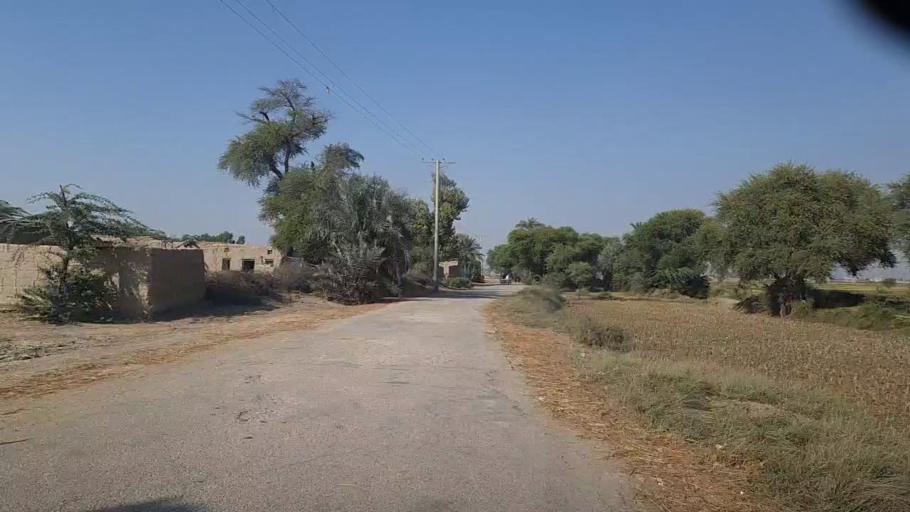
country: PK
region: Sindh
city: Tangwani
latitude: 28.2455
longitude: 68.9963
